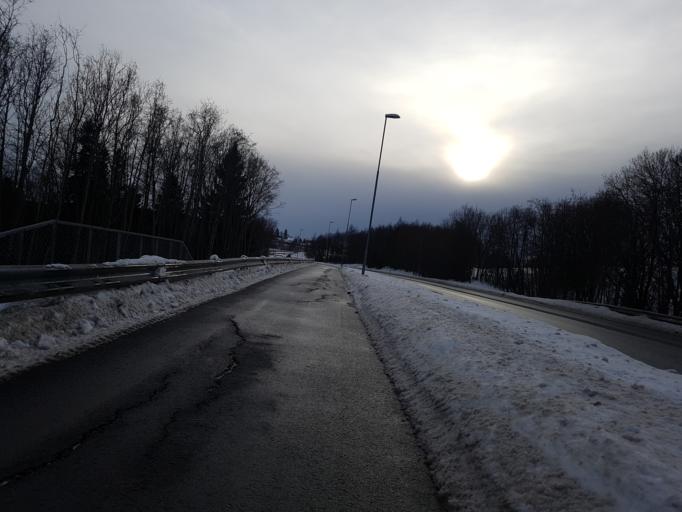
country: NO
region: Sor-Trondelag
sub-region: Trondheim
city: Trondheim
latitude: 63.3737
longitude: 10.3811
